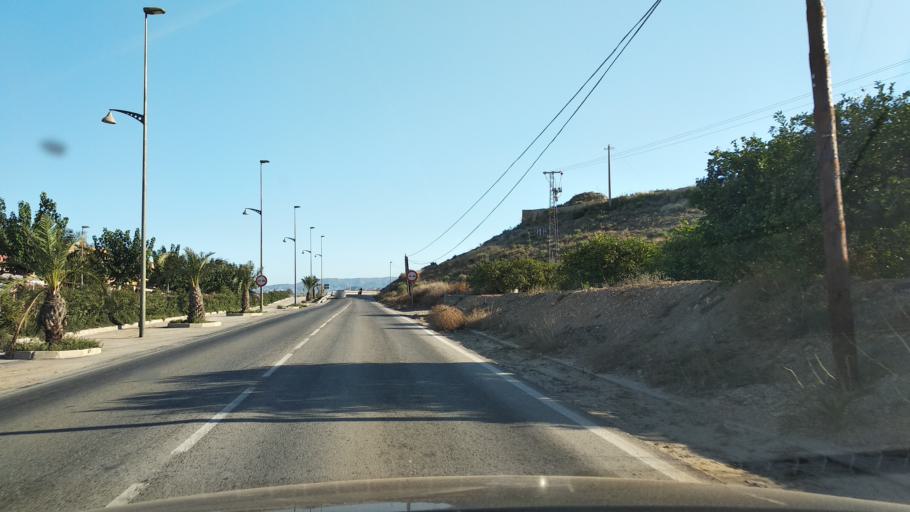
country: ES
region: Murcia
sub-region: Murcia
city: Santomera
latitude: 38.0576
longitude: -1.0531
